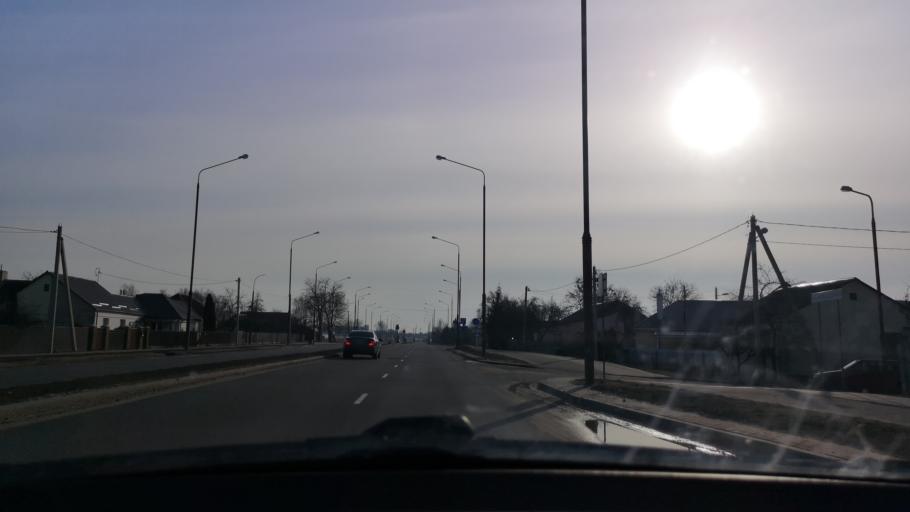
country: BY
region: Brest
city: Brest
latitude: 52.1169
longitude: 23.6695
